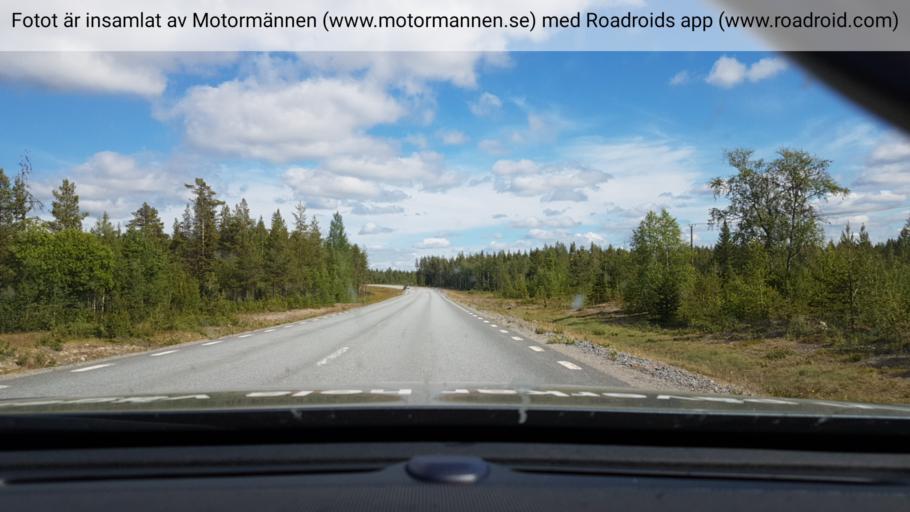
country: SE
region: Vaesterbotten
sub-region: Sorsele Kommun
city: Sorsele
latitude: 65.5576
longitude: 17.7534
